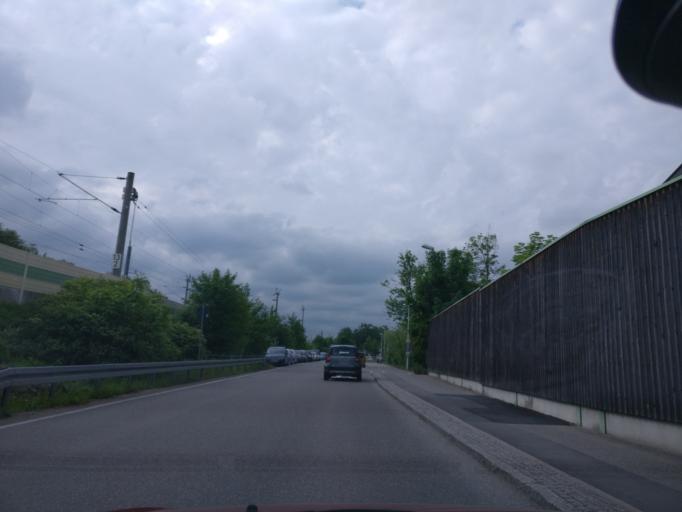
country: DE
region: Bavaria
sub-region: Upper Bavaria
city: Karlsfeld
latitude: 48.2148
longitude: 11.4580
